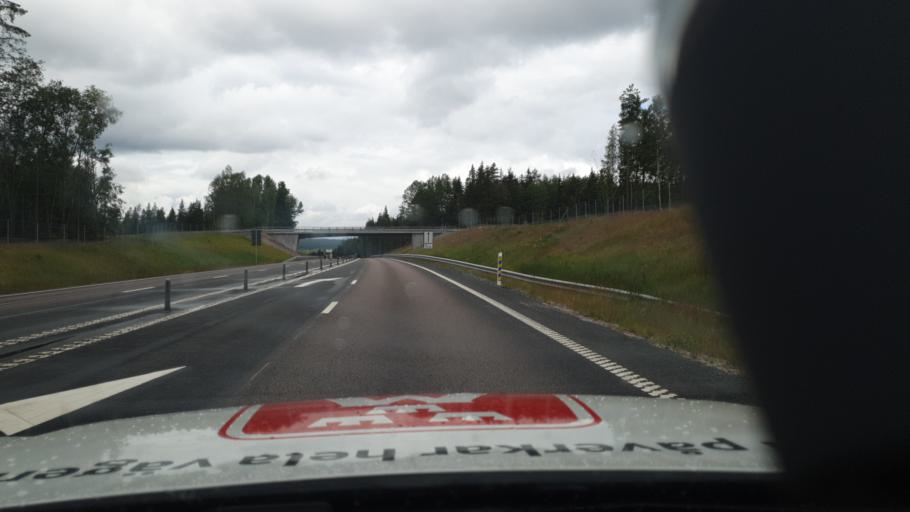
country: SE
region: Joenkoeping
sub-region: Mullsjo Kommun
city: Mullsjoe
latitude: 57.8933
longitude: 13.8838
